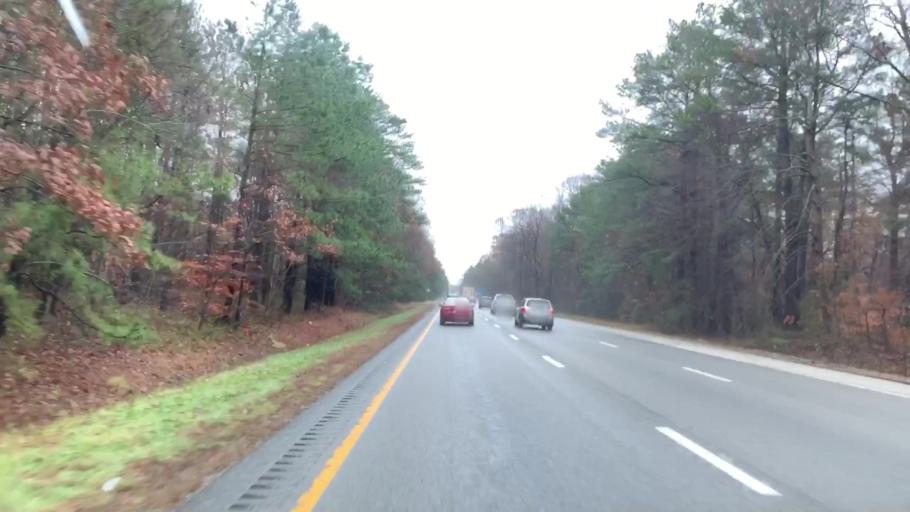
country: US
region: Virginia
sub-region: James City County
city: Williamsburg
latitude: 37.3797
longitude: -76.7580
